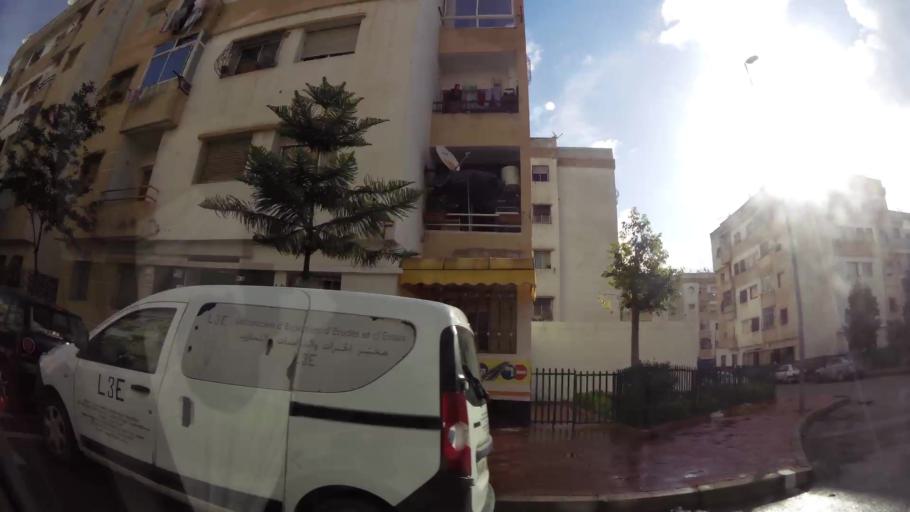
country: MA
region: Grand Casablanca
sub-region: Mediouna
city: Tit Mellil
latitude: 33.6004
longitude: -7.5329
